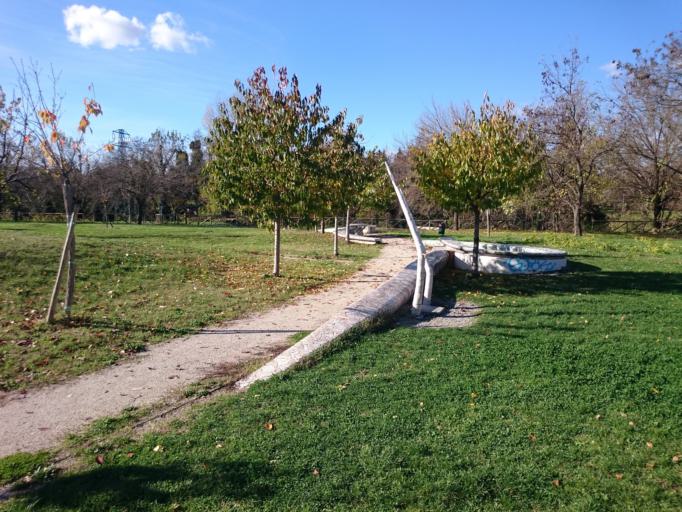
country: IT
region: Emilia-Romagna
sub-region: Provincia di Bologna
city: Bologna
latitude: 44.5139
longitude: 11.3341
